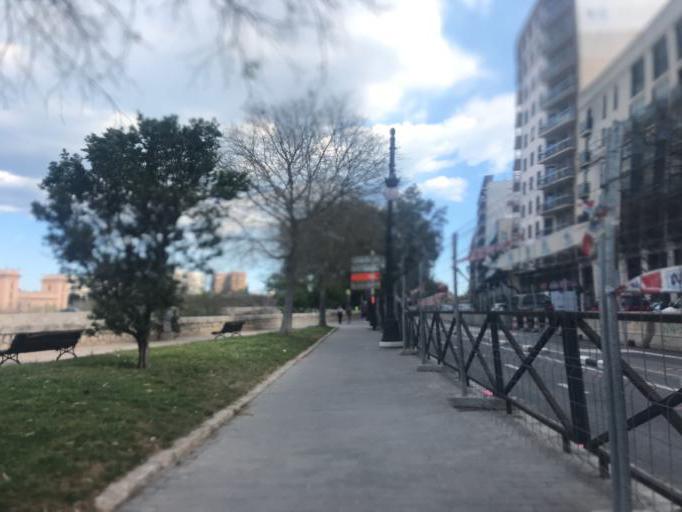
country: ES
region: Valencia
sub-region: Provincia de Valencia
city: Valencia
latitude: 39.4788
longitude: -0.3741
